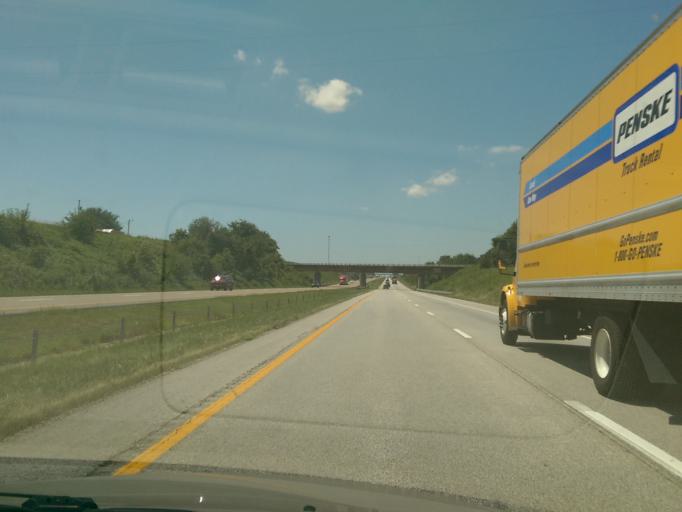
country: US
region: Missouri
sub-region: Cooper County
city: Boonville
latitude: 38.9353
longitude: -92.7992
